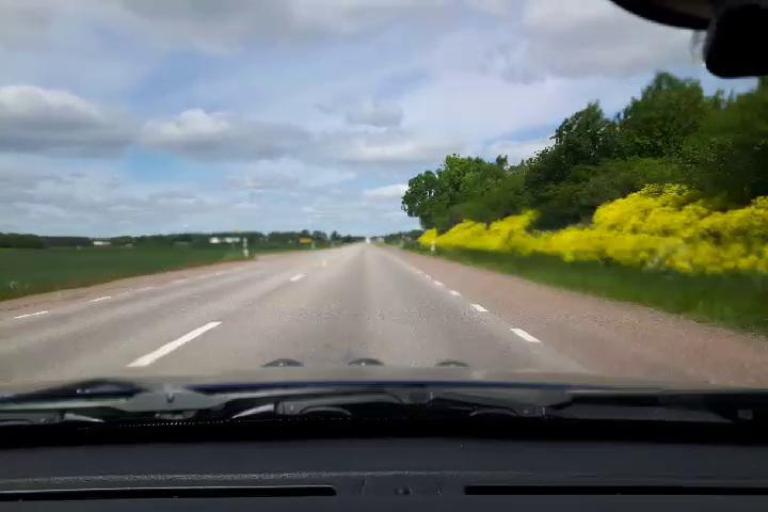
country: SE
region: Uppsala
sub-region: Uppsala Kommun
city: Gamla Uppsala
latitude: 59.9193
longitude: 17.6038
